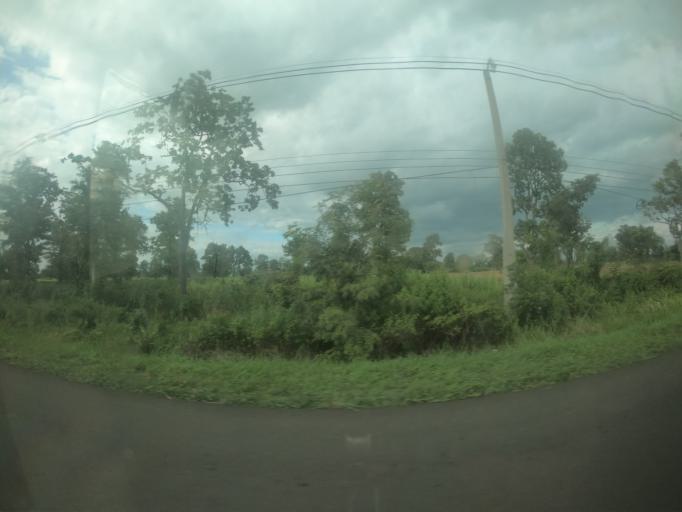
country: TH
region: Surin
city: Kap Choeng
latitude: 14.5432
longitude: 103.5175
